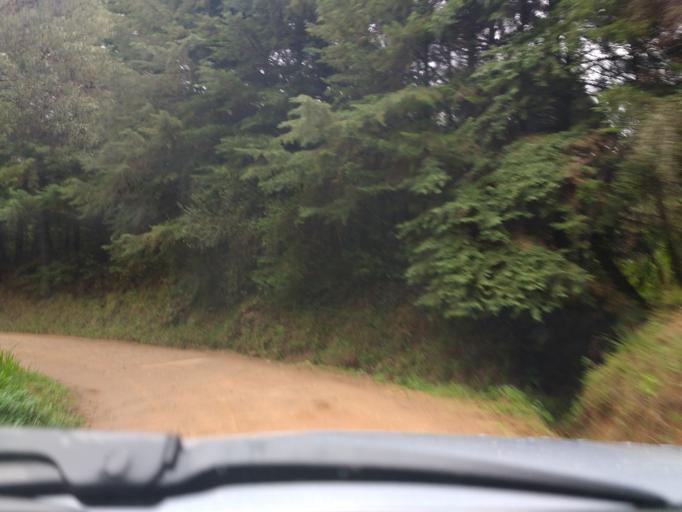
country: BR
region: Minas Gerais
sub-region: Cambui
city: Cambui
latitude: -22.7449
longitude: -45.9165
